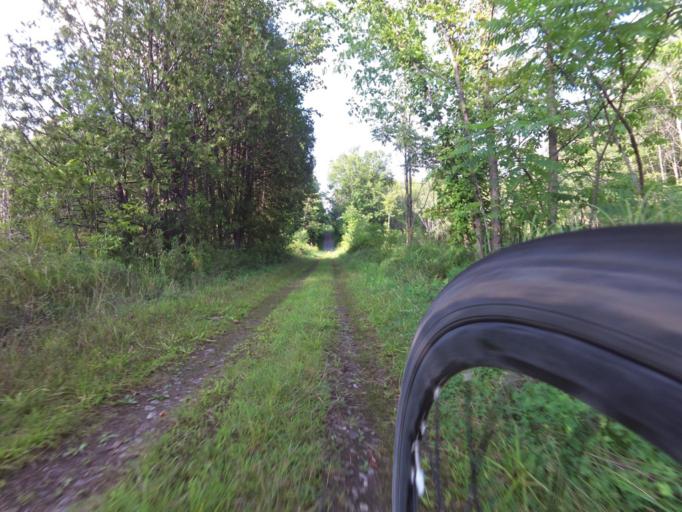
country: CA
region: Ontario
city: Kingston
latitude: 44.4823
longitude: -76.4771
